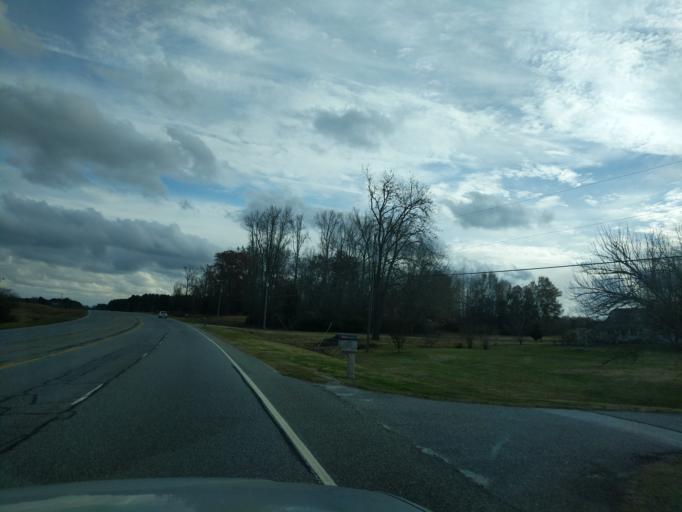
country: US
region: South Carolina
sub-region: Greenwood County
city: Ware Shoals
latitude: 34.4880
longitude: -82.2841
